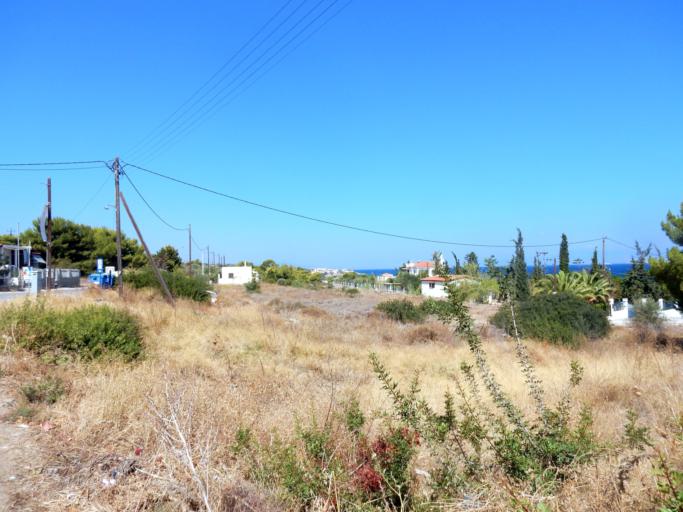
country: GR
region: Attica
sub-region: Nomos Piraios
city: Vathi
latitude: 37.7709
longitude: 23.5250
